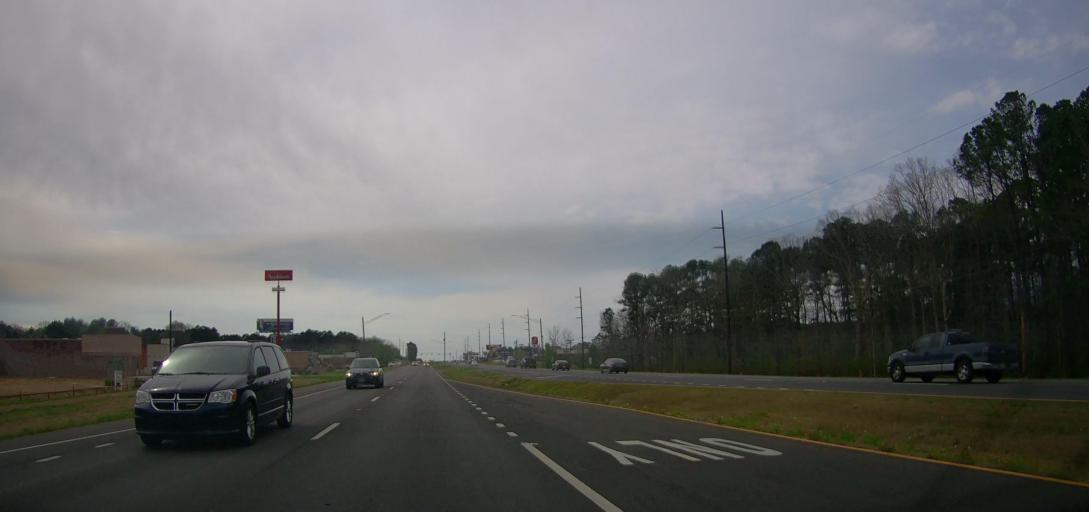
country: US
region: Alabama
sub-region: Walker County
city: Jasper
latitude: 33.8439
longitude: -87.2494
